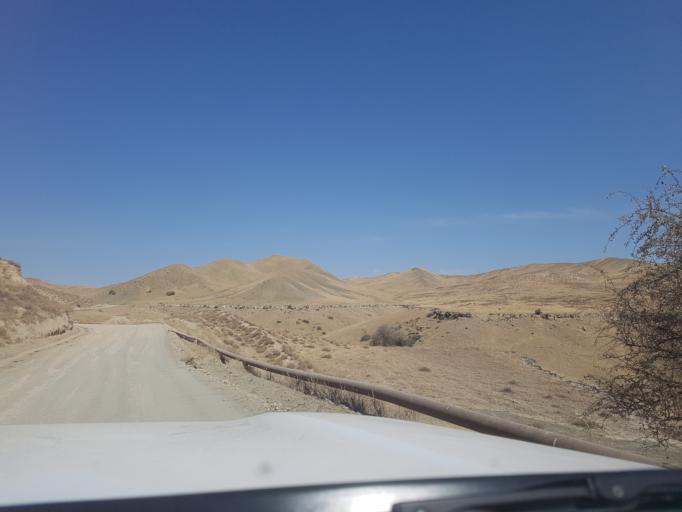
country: TM
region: Ahal
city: Baharly
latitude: 38.2520
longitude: 56.8910
